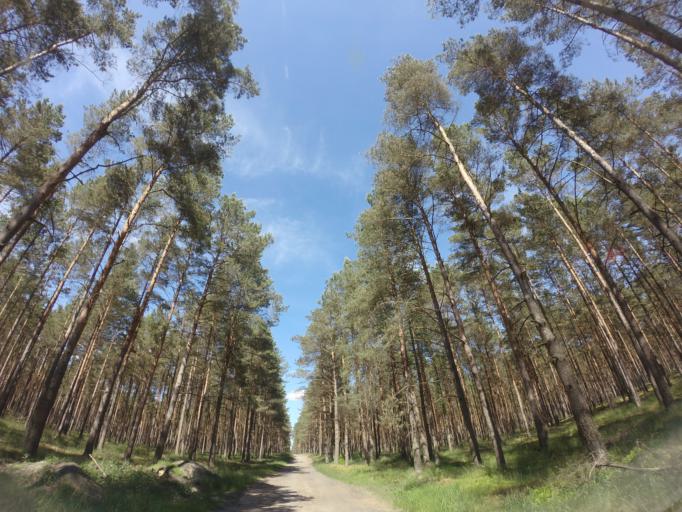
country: PL
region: West Pomeranian Voivodeship
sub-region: Powiat choszczenski
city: Drawno
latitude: 53.1520
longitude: 15.7837
